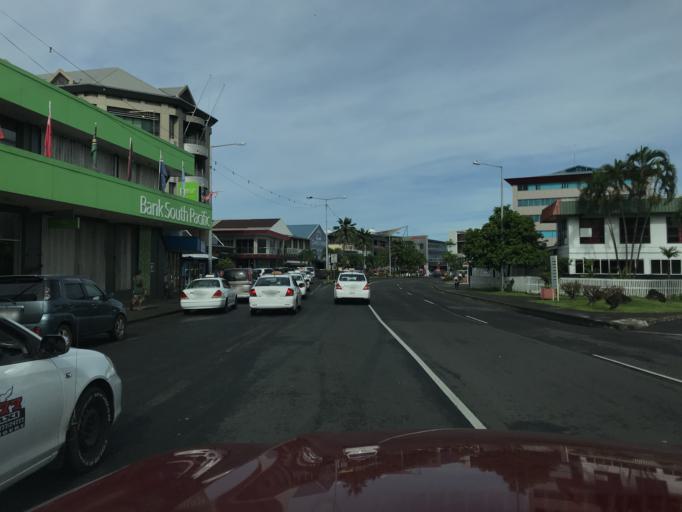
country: WS
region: Tuamasaga
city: Apia
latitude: -13.8305
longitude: -171.7691
